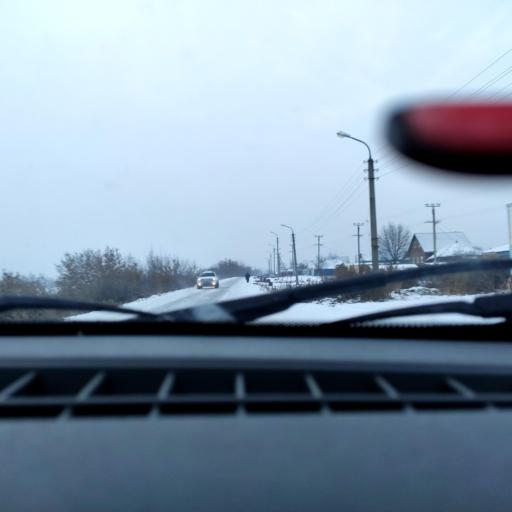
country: RU
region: Bashkortostan
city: Blagoveshchensk
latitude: 54.8938
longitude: 56.0291
